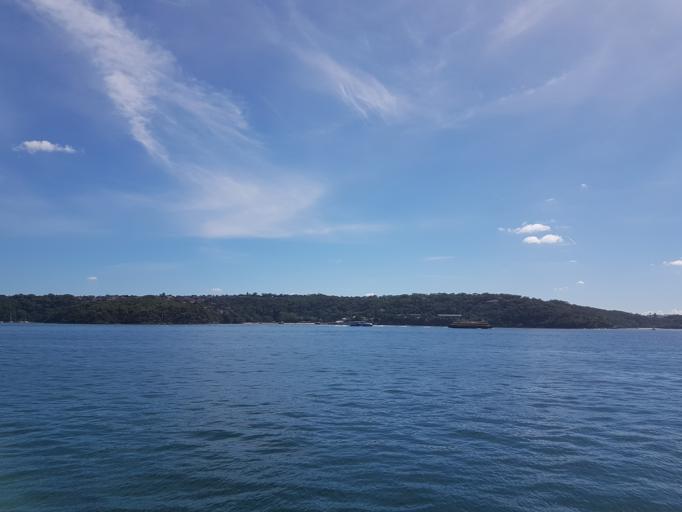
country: AU
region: New South Wales
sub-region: Woollahra
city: Point Piper
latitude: -33.8488
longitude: 151.2641
